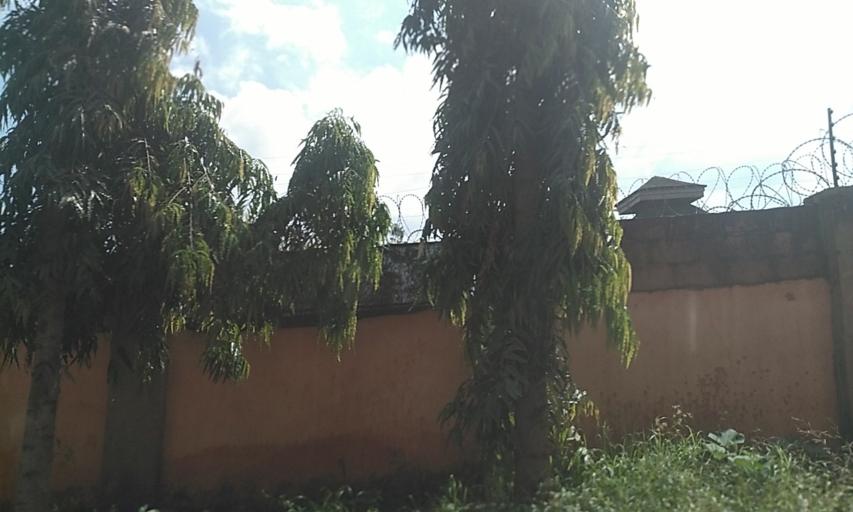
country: UG
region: Central Region
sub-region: Wakiso District
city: Kireka
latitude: 0.3492
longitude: 32.6120
